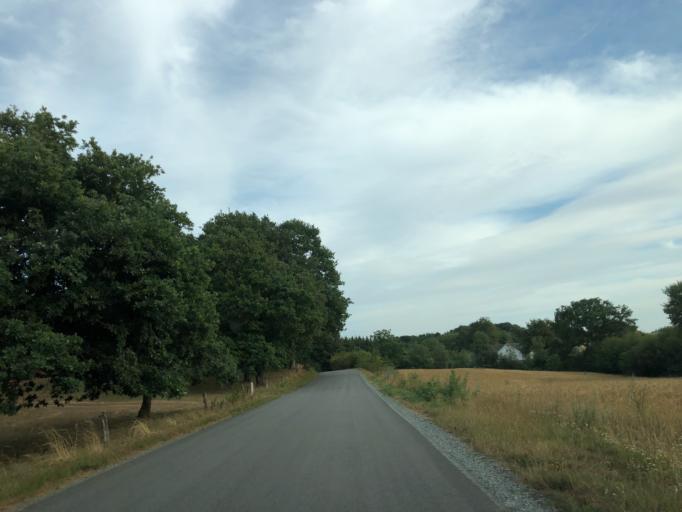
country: DK
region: South Denmark
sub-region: Vejle Kommune
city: Egtved
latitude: 55.6824
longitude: 9.2653
